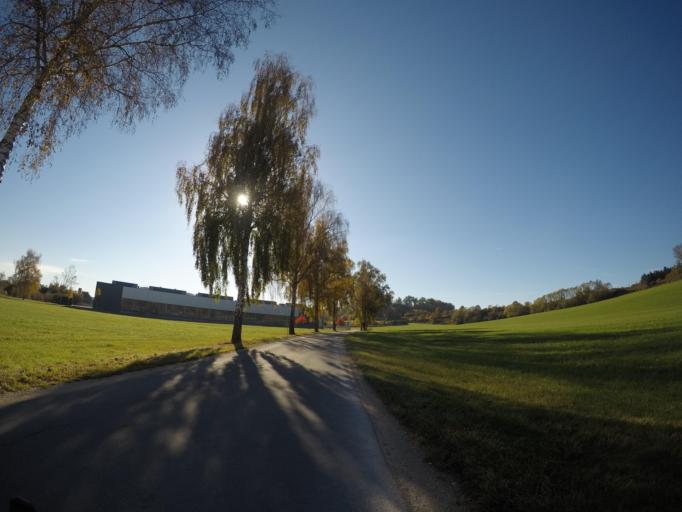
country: DE
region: Baden-Wuerttemberg
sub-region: Tuebingen Region
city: Saulgau
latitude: 48.0282
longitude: 9.4826
